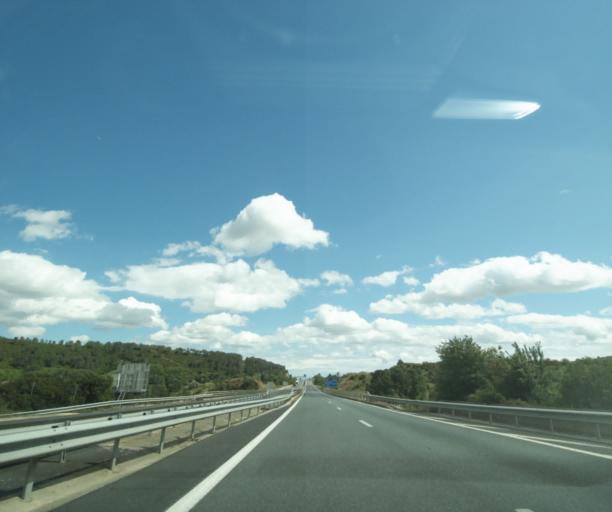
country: FR
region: Languedoc-Roussillon
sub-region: Departement de l'Herault
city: Nebian
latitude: 43.6673
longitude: 3.4309
